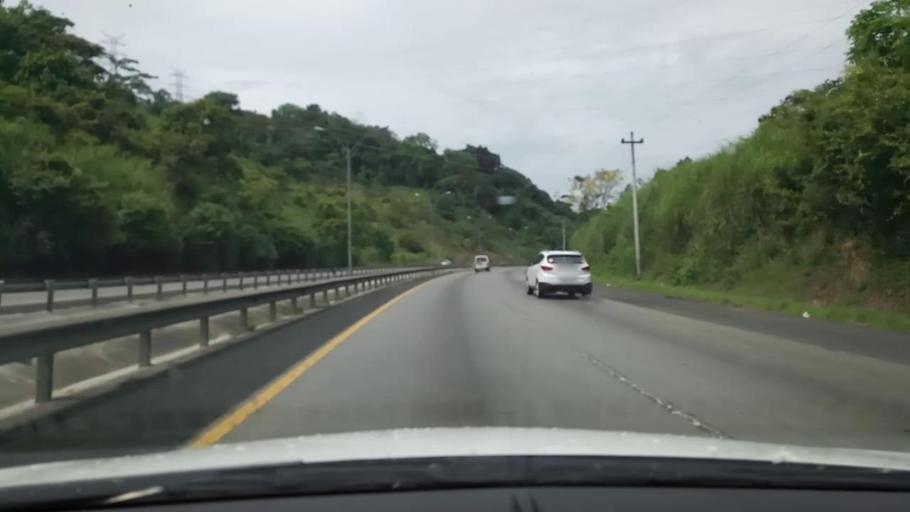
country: PA
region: Panama
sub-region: Distrito de Panama
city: Paraiso
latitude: 9.0279
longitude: -79.6123
